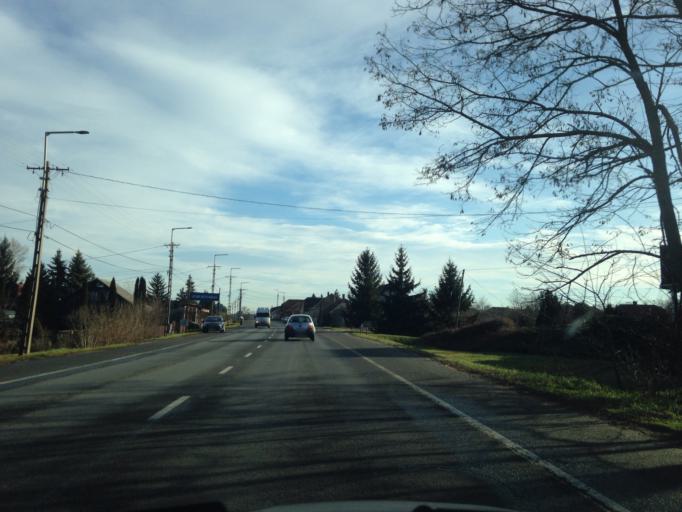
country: HU
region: Gyor-Moson-Sopron
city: Abda
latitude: 47.7032
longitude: 17.5305
